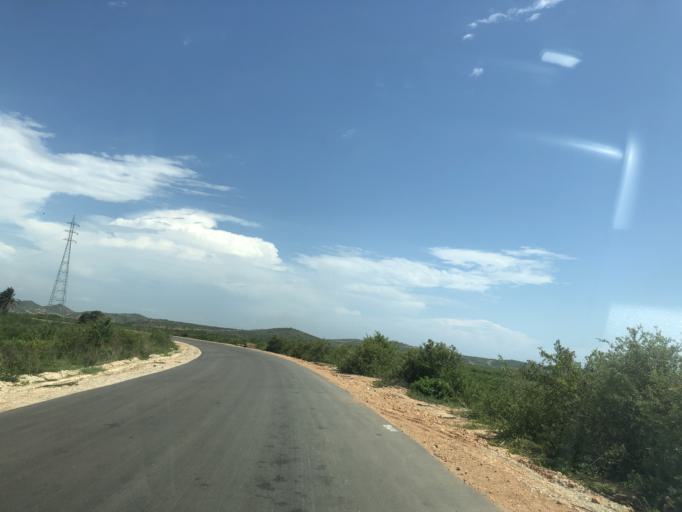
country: AO
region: Cuanza Sul
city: Sumbe
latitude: -10.8795
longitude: 13.8396
